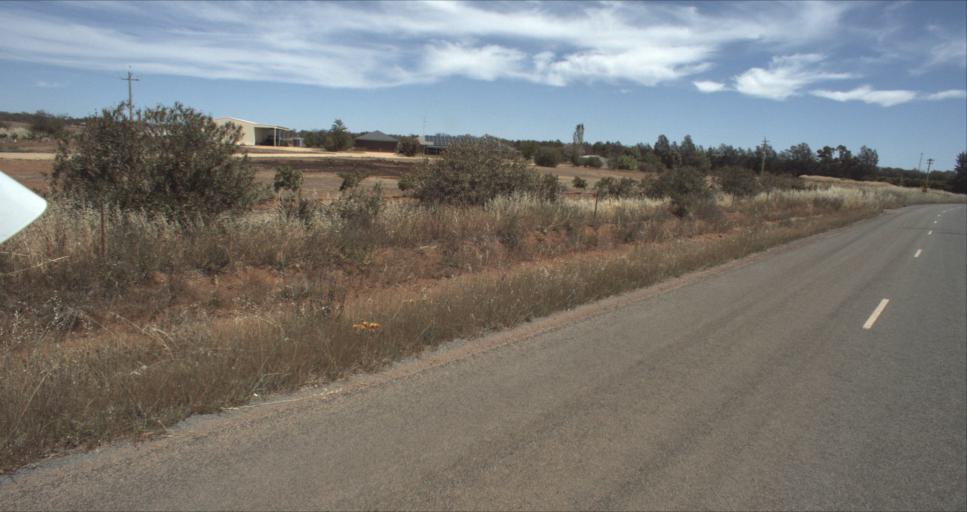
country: AU
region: New South Wales
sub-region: Leeton
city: Leeton
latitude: -34.5929
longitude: 146.4697
